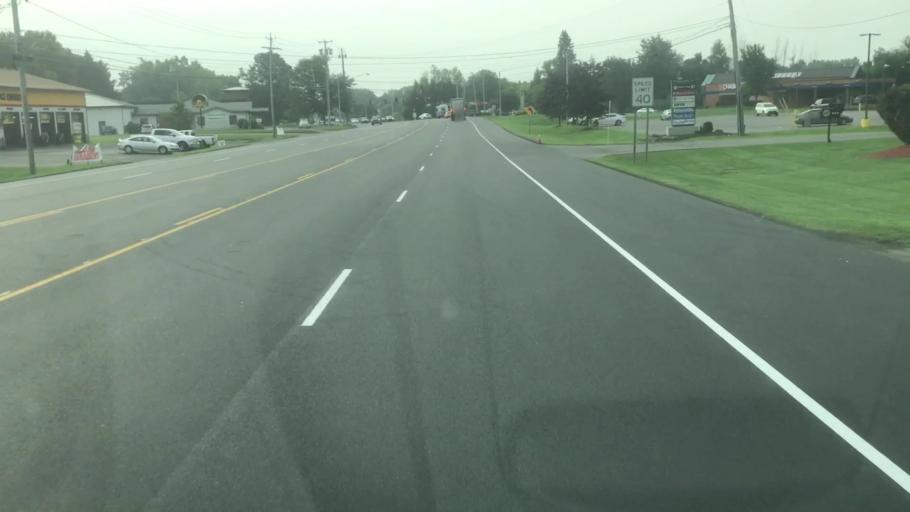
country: US
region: New York
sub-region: Onondaga County
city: Liverpool
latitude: 43.1380
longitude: -76.2263
